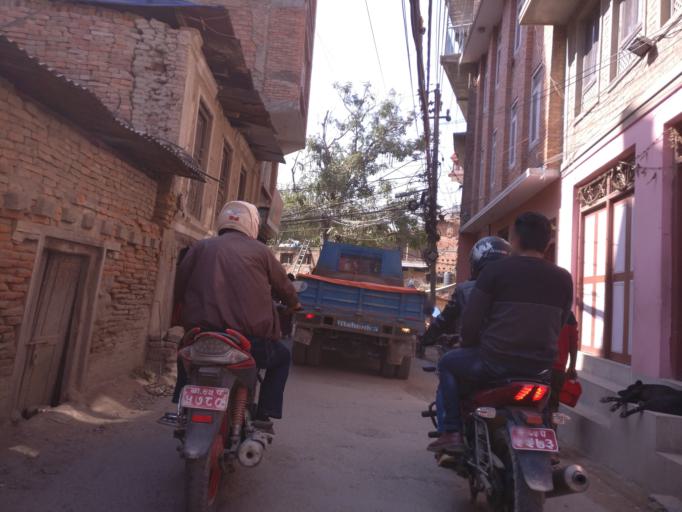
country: NP
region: Central Region
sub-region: Bagmati Zone
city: Patan
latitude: 27.6766
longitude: 85.3270
